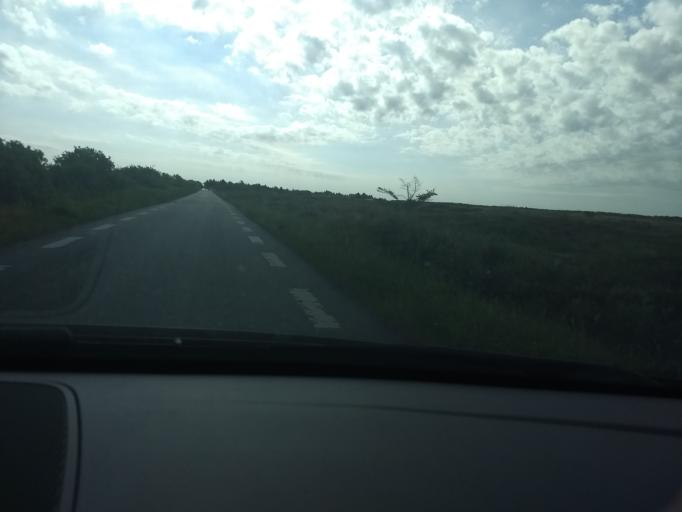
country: DE
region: Schleswig-Holstein
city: List
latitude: 55.1310
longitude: 8.5136
